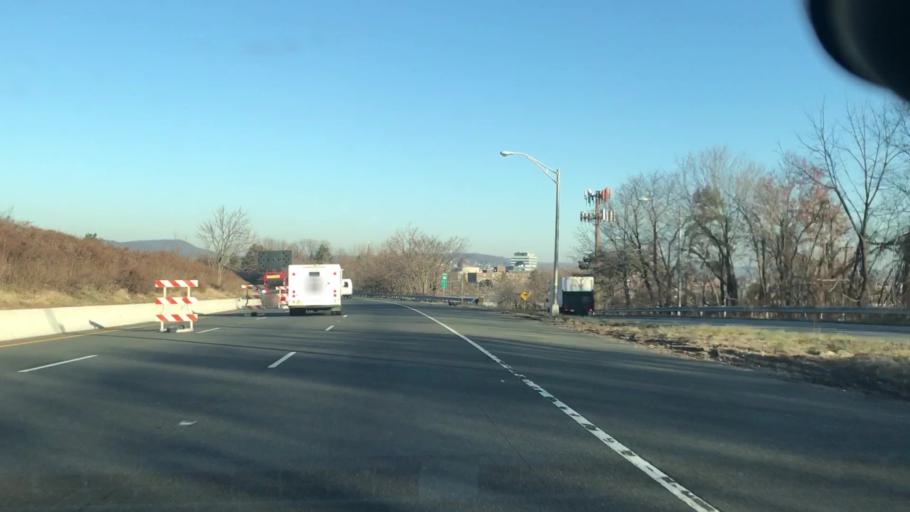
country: US
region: New Jersey
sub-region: Passaic County
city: Paterson
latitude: 40.9047
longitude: -74.1713
